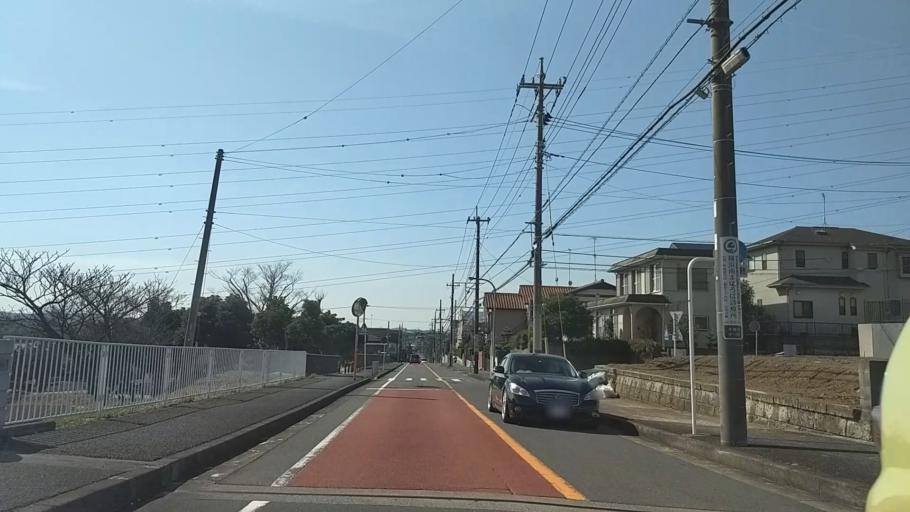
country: JP
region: Kanagawa
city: Kamakura
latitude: 35.3791
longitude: 139.5504
